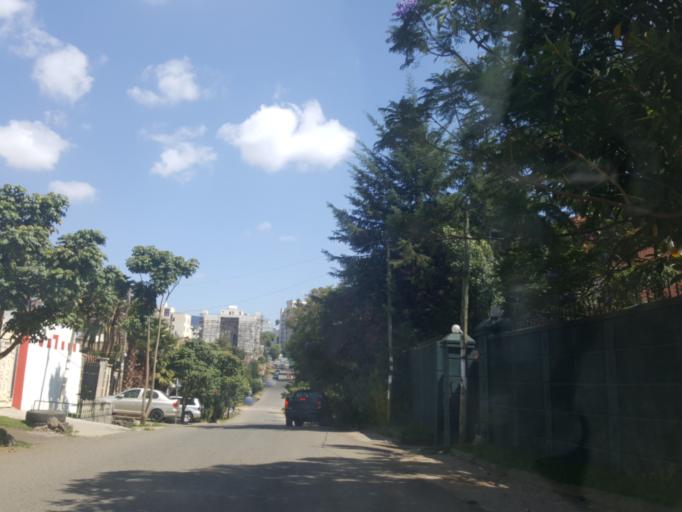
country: ET
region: Adis Abeba
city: Addis Ababa
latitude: 9.0551
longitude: 38.7363
